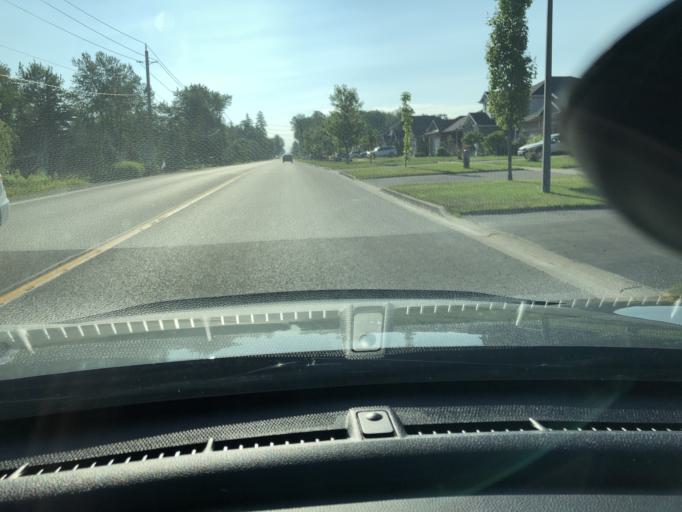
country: CA
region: Ontario
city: Stratford
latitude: 43.3893
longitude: -80.9614
